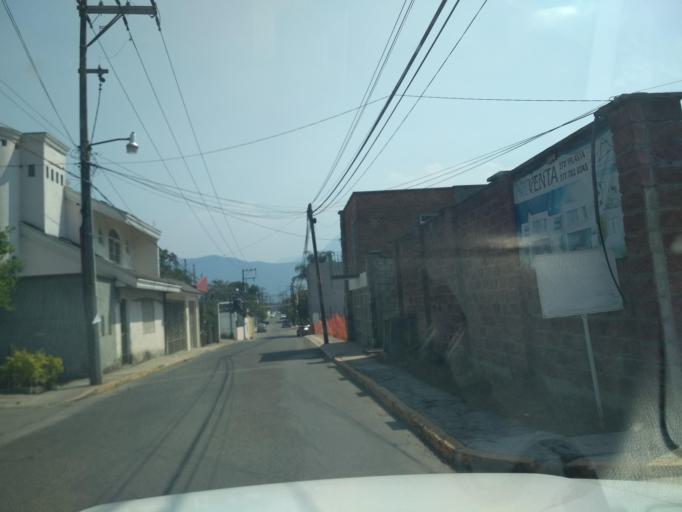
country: MX
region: Veracruz
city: Orizaba
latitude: 18.8423
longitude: -97.0856
